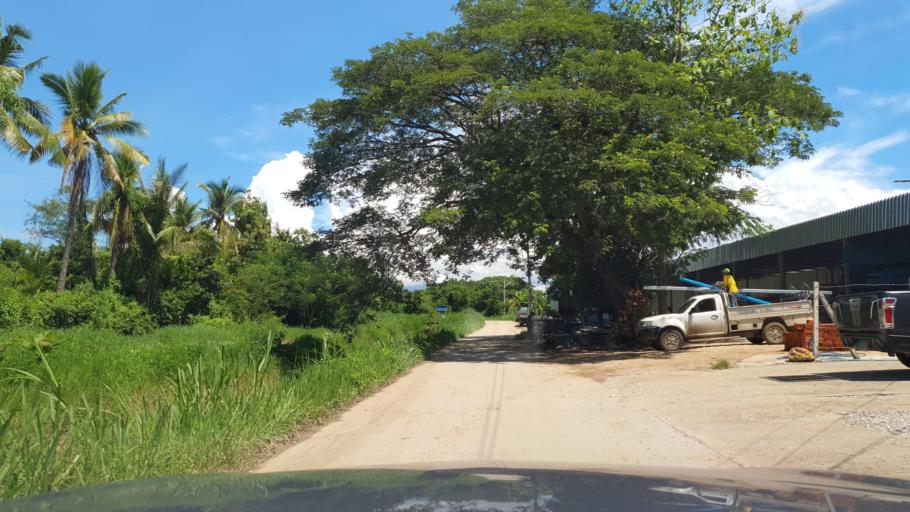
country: TH
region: Chiang Mai
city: San Kamphaeng
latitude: 18.7289
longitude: 99.1278
